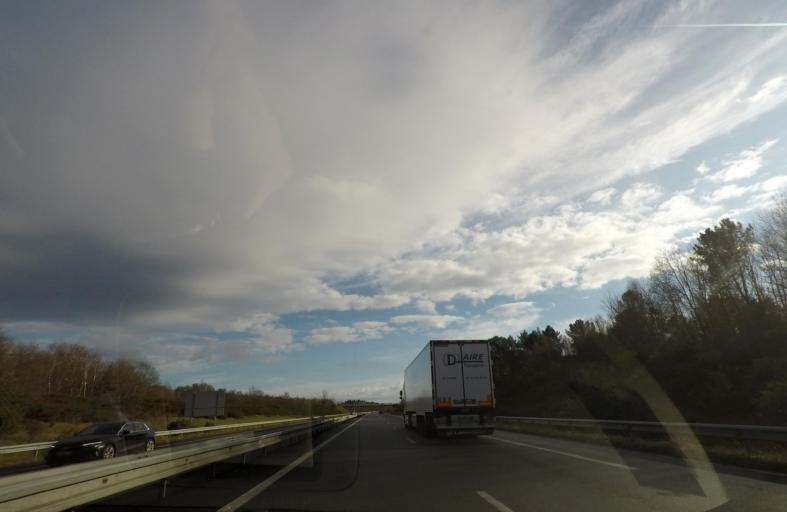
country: FR
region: Centre
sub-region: Departement du Loir-et-Cher
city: Villefranche-sur-Cher
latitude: 47.3091
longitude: 1.8405
